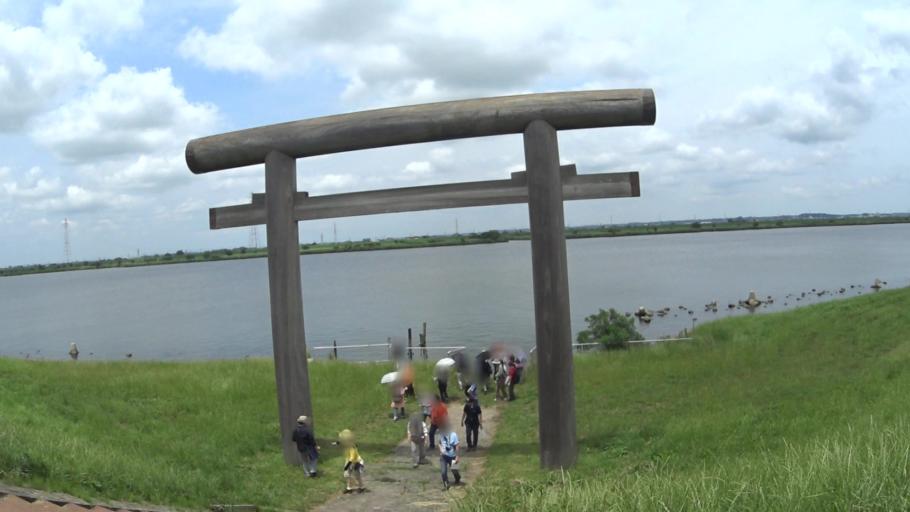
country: JP
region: Chiba
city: Katori-shi
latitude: 35.9015
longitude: 140.5262
